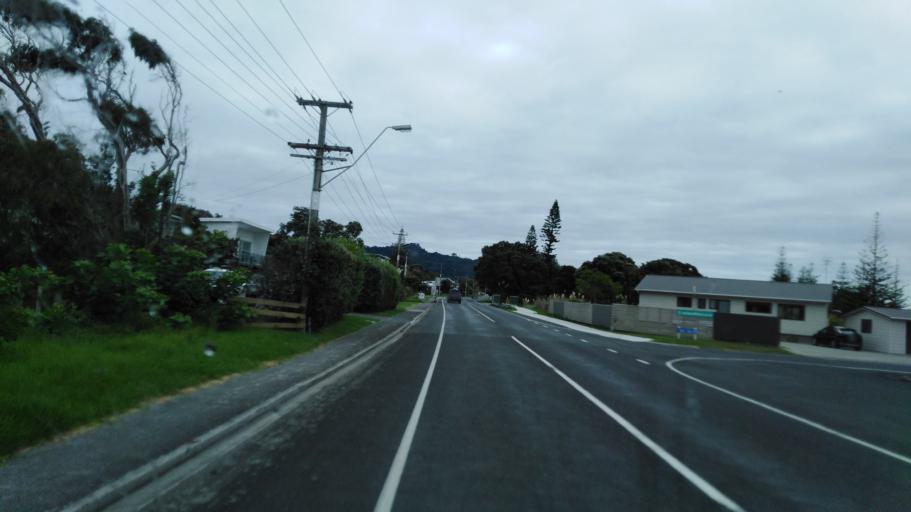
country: NZ
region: Bay of Plenty
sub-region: Western Bay of Plenty District
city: Waihi Beach
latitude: -37.4197
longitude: 175.9520
